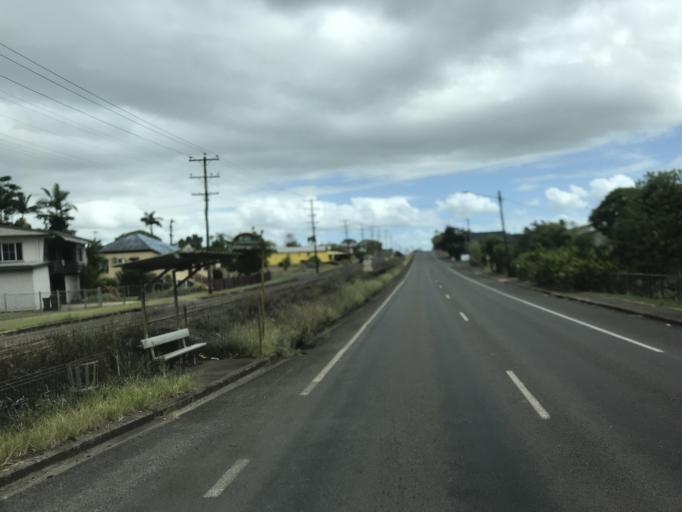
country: AU
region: Queensland
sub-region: Cassowary Coast
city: Innisfail
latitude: -17.5980
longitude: 145.9951
